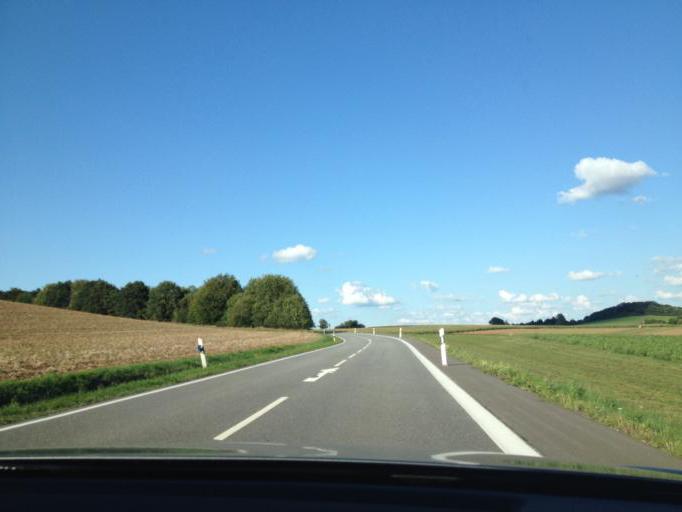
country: DE
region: Saarland
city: Tholey
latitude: 49.4795
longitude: 6.9743
